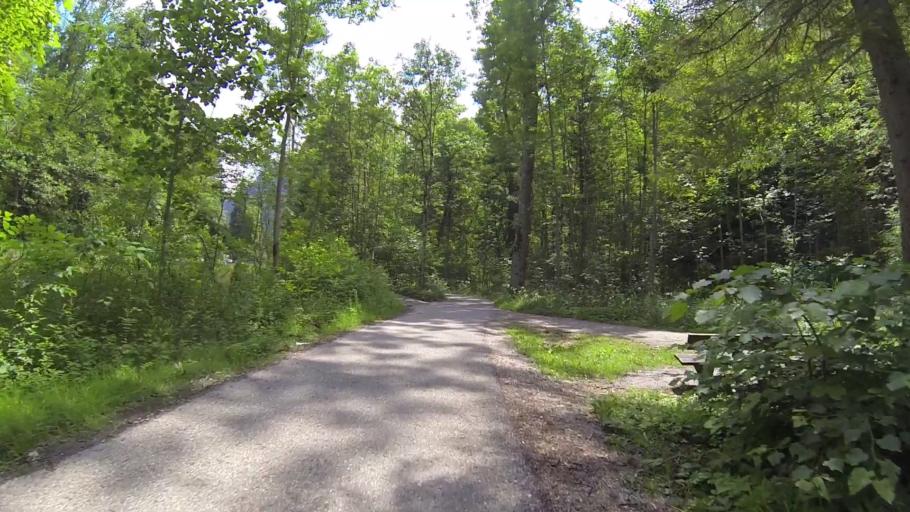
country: DE
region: Bavaria
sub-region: Swabia
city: Schwangau
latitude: 47.5569
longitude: 10.7358
